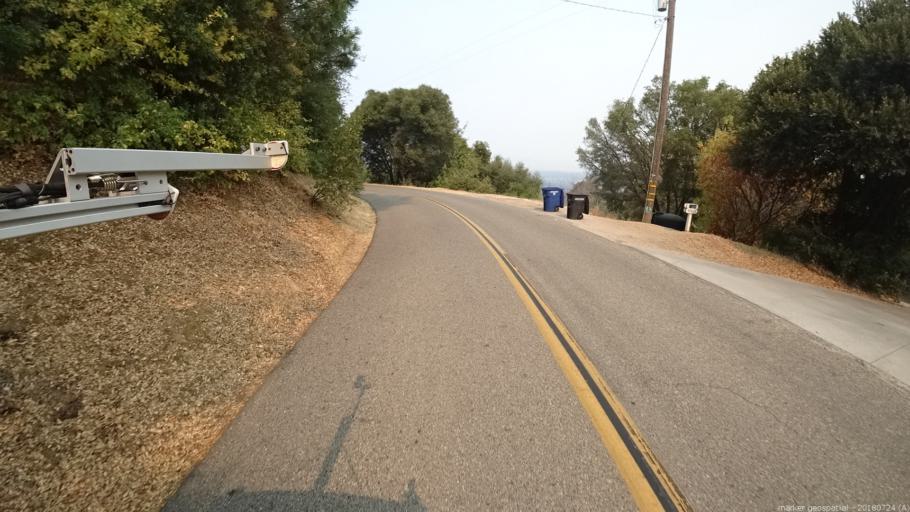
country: US
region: California
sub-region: Madera County
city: Oakhurst
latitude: 37.3160
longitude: -119.6160
